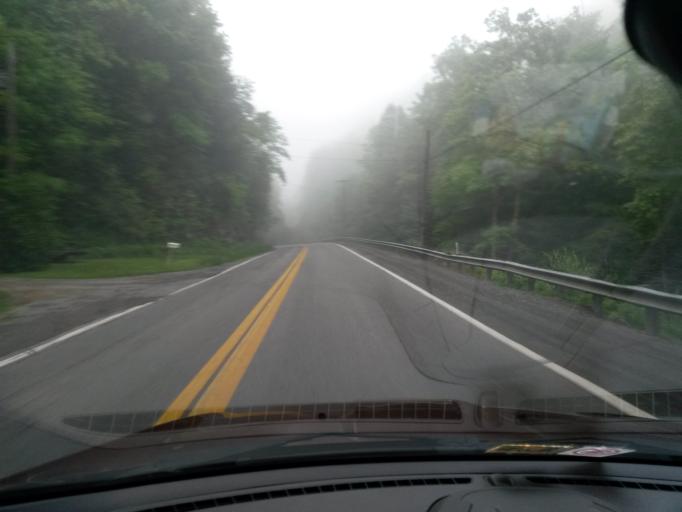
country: US
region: West Virginia
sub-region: McDowell County
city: Welch
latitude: 37.4553
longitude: -81.5433
